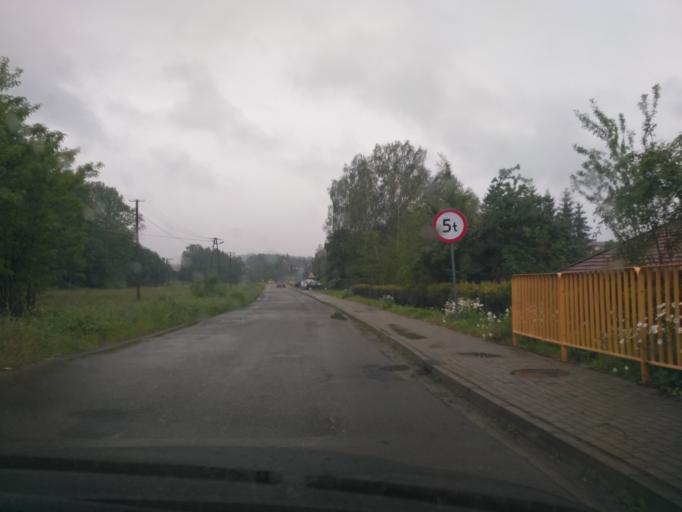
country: PL
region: Subcarpathian Voivodeship
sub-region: Powiat krosnienski
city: Leki
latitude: 49.7920
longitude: 21.6538
